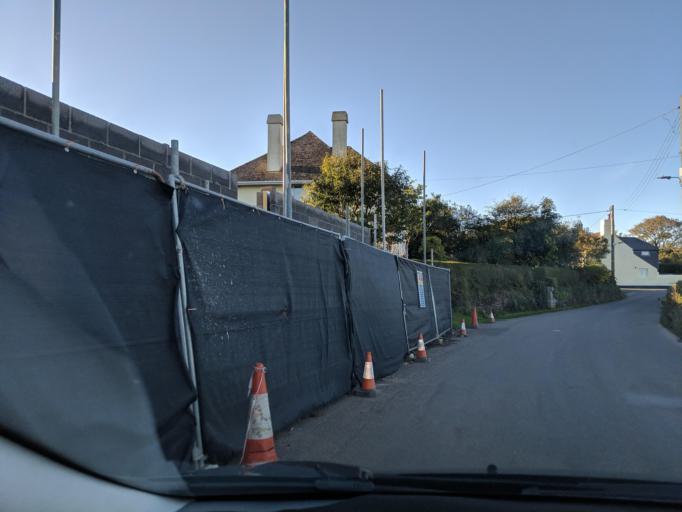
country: GB
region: England
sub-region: Plymouth
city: Plymstock
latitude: 50.3328
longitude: -4.1040
